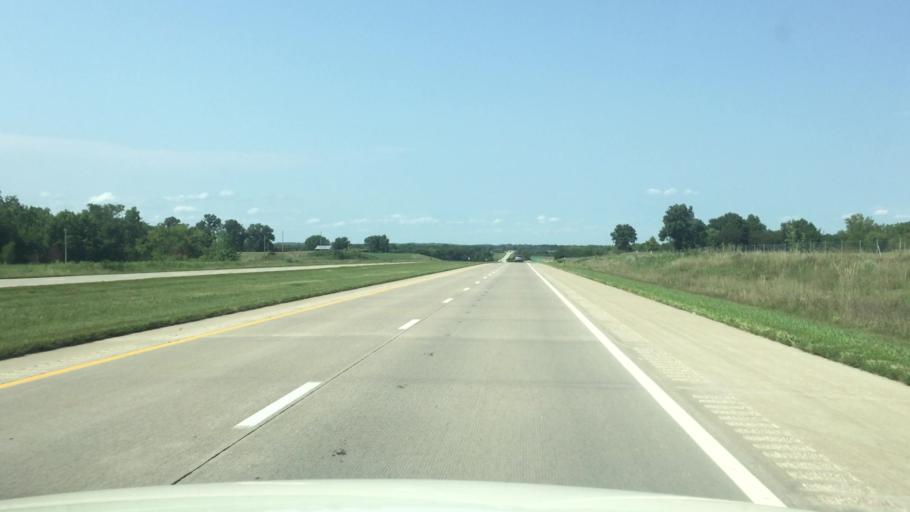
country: US
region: Kansas
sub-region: Linn County
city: Pleasanton
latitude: 38.1255
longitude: -94.7133
